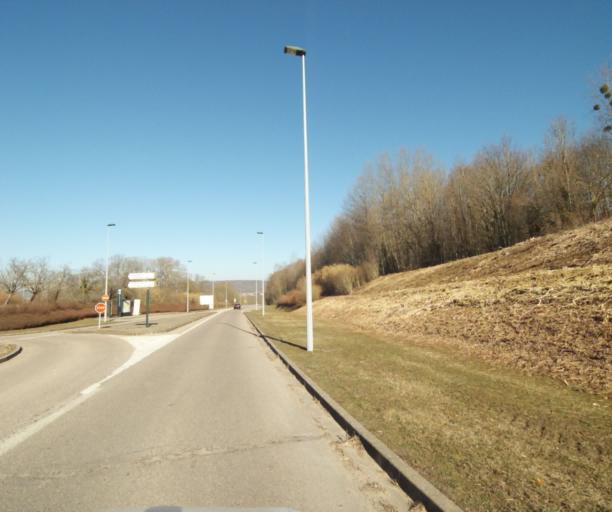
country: FR
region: Lorraine
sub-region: Departement de Meurthe-et-Moselle
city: Champigneulles
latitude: 48.7320
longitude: 6.1831
